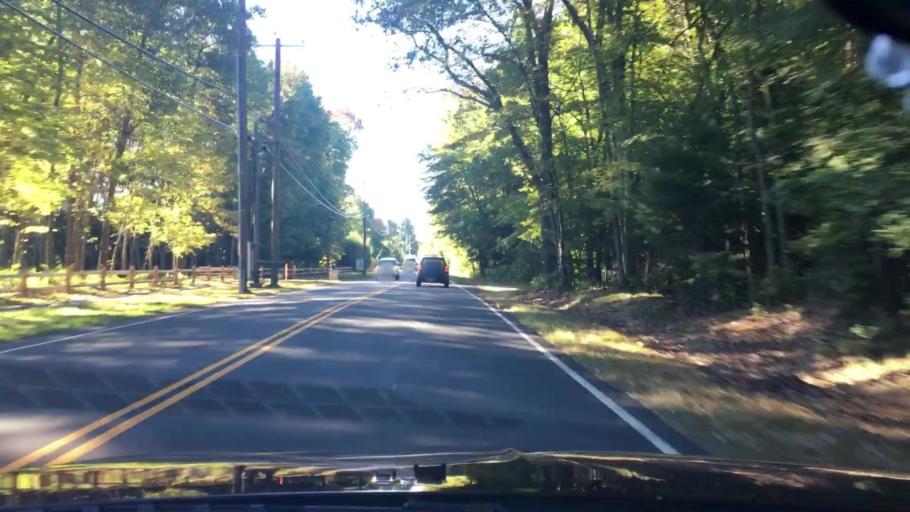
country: US
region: Connecticut
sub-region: Hartford County
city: Sherwood Manor
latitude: 42.0098
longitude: -72.5593
